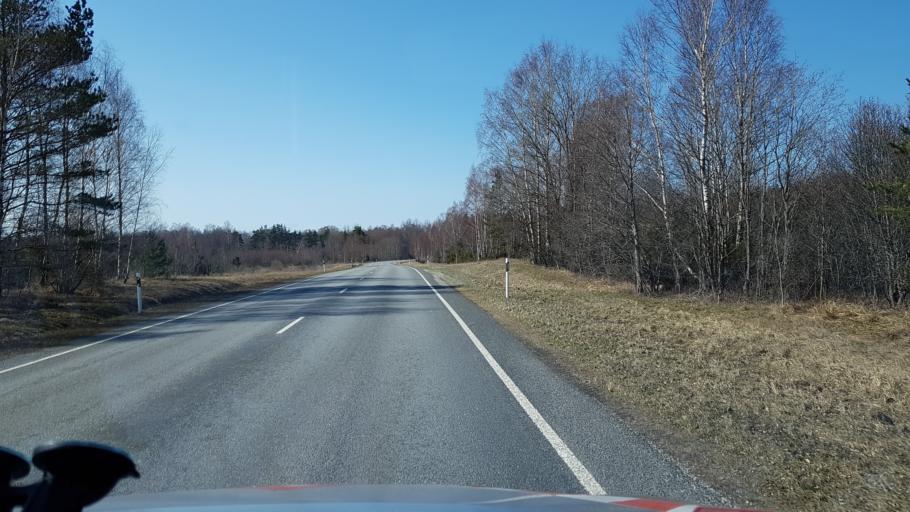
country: EE
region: Laeaene
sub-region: Haapsalu linn
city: Haapsalu
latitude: 58.9113
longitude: 23.4531
